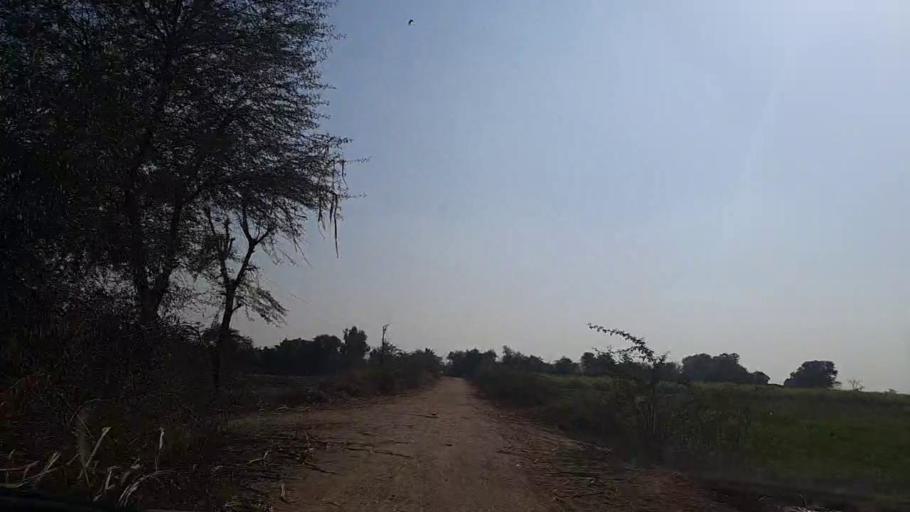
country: PK
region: Sindh
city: Sakrand
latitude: 26.0762
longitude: 68.3694
